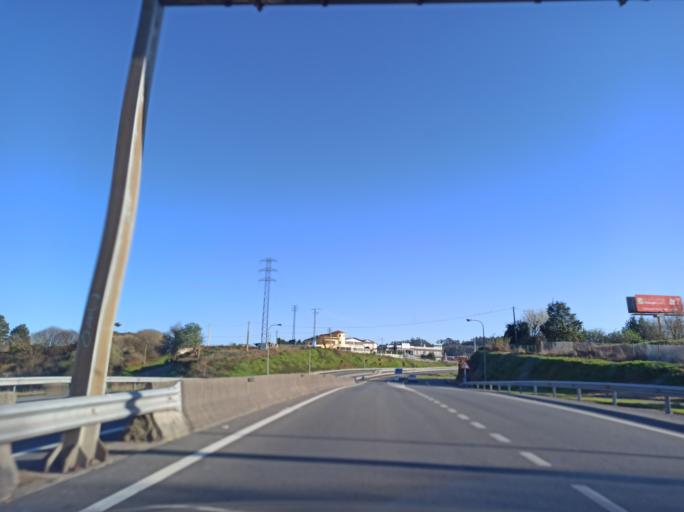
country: ES
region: Galicia
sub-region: Provincia da Coruna
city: Cambre
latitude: 43.3139
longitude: -8.3541
